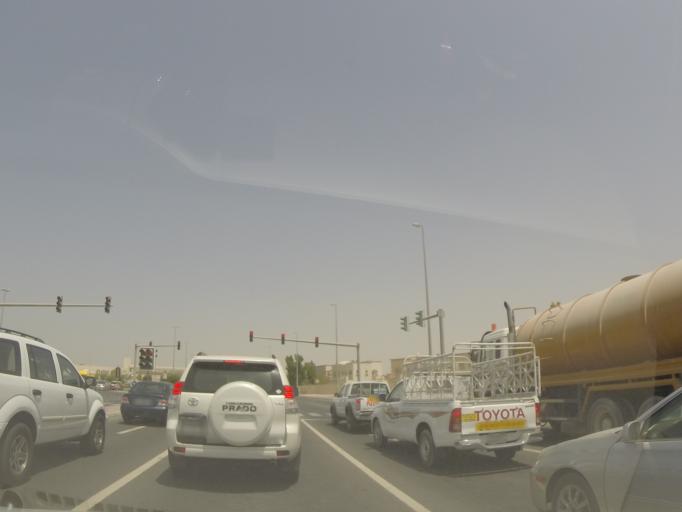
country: AE
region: Dubai
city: Dubai
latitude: 25.0550
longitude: 55.1736
